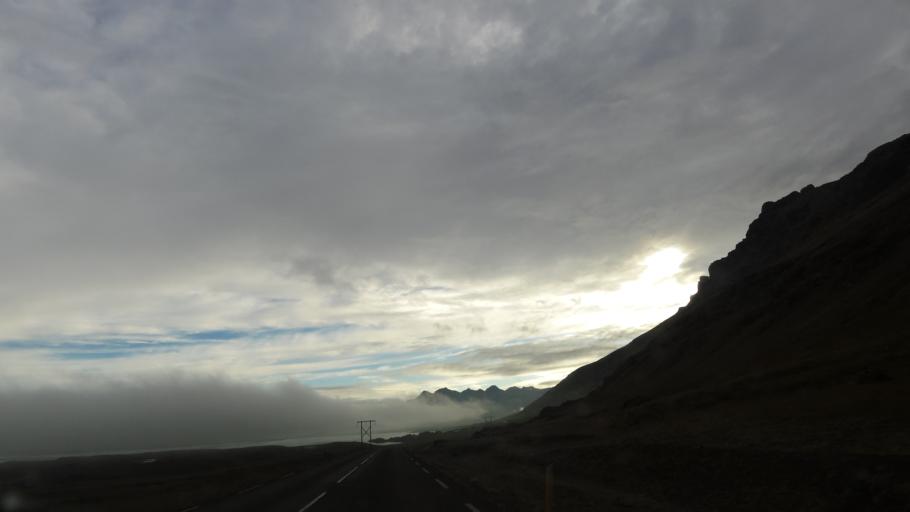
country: IS
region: East
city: Reydarfjoerdur
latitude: 64.5975
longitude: -14.4656
